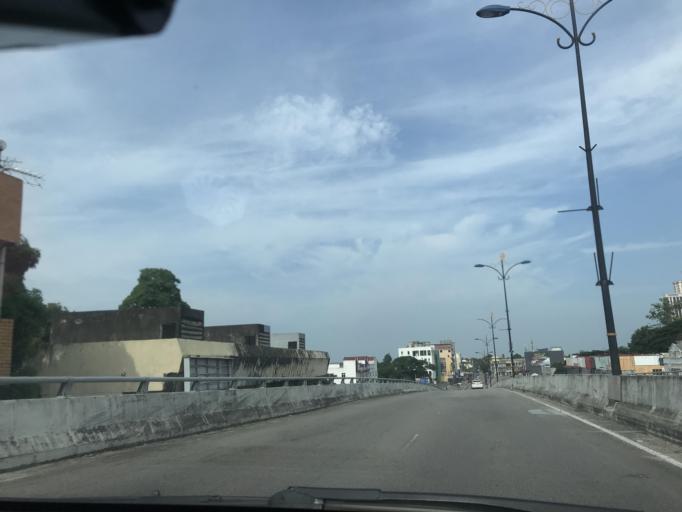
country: MY
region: Kelantan
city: Kota Bharu
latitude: 6.1173
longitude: 102.2431
